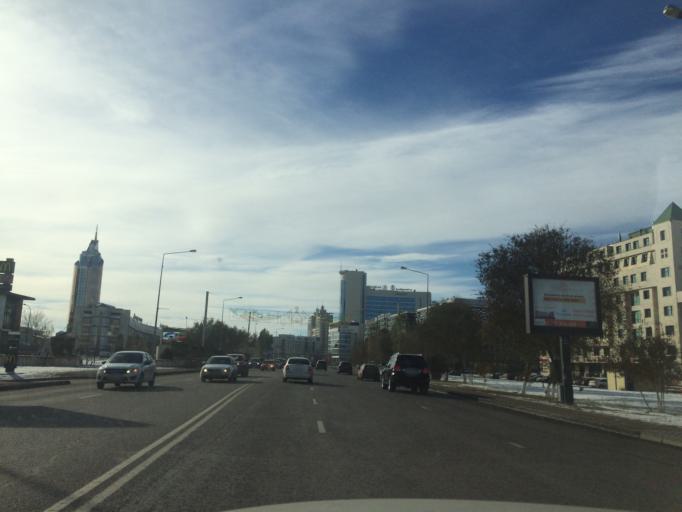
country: KZ
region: Astana Qalasy
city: Astana
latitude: 51.1380
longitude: 71.4167
